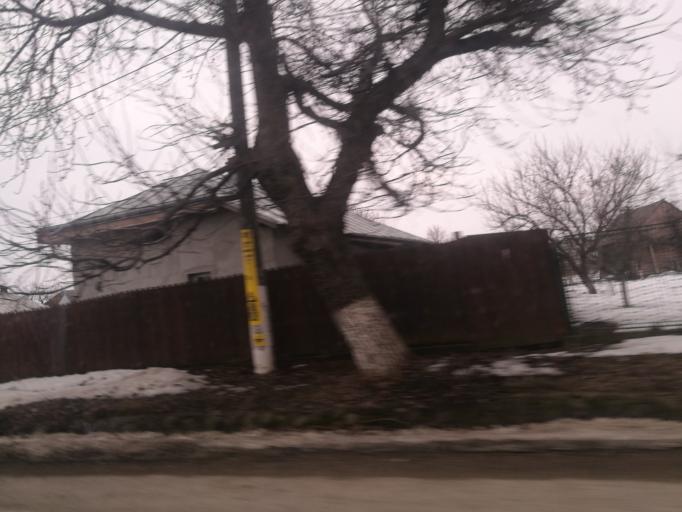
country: RO
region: Iasi
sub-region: Comuna Ruginoasa
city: Dumbravita
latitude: 47.2403
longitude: 26.8305
